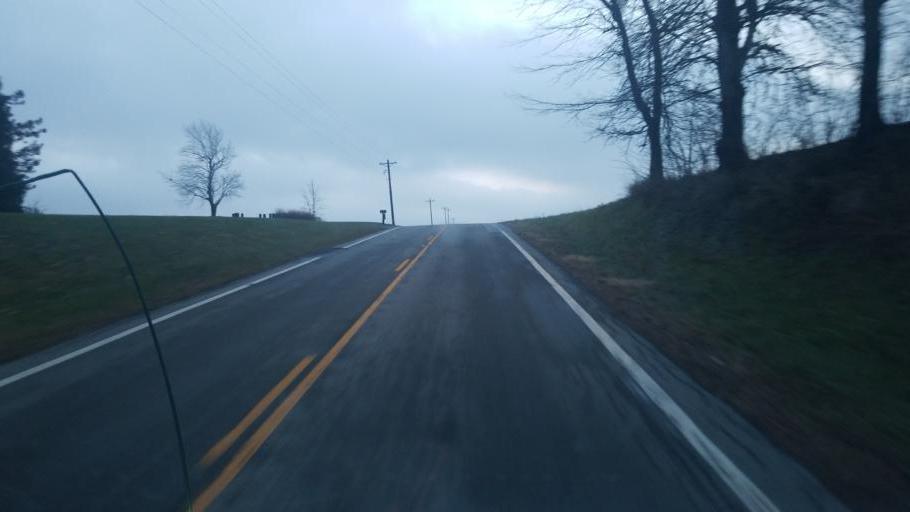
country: US
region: Ohio
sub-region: Seneca County
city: Tiffin
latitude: 40.9381
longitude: -83.1315
